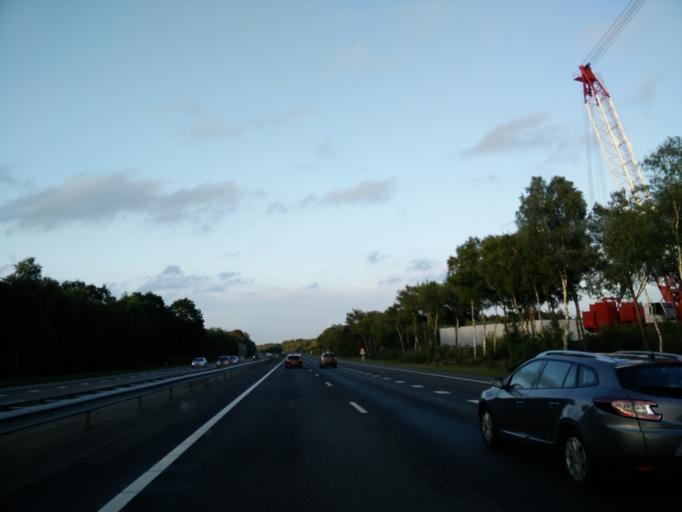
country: NL
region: Gelderland
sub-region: Gemeente Oldebroek
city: Oldebroek
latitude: 52.4123
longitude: 5.8958
